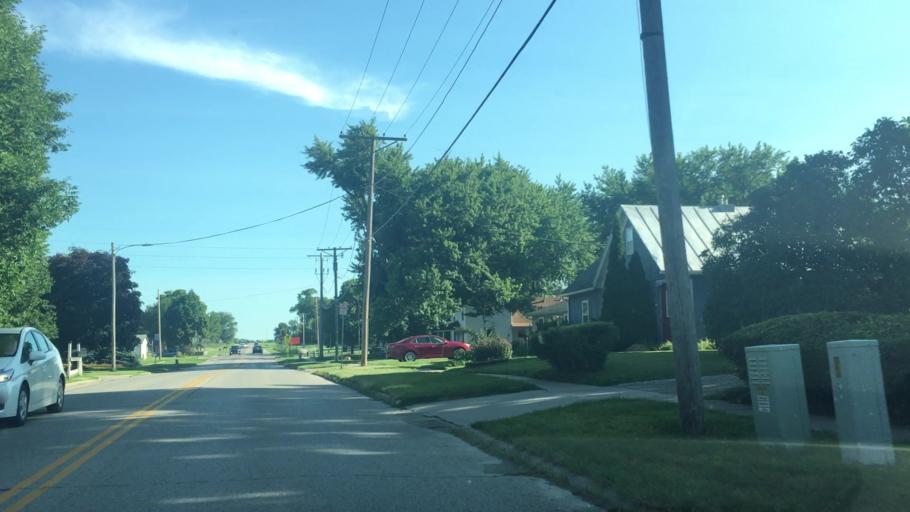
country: US
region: Iowa
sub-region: Johnson County
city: North Liberty
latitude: 41.7508
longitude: -91.5980
